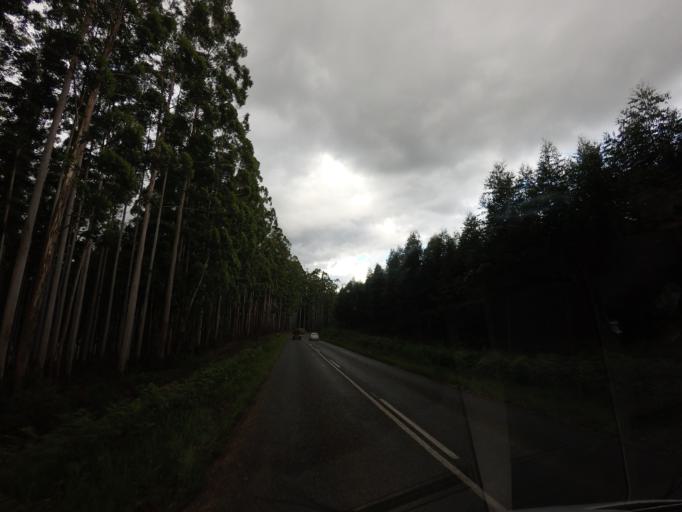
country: ZA
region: Mpumalanga
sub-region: Ehlanzeni District
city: Graksop
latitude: -24.9562
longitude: 30.8994
